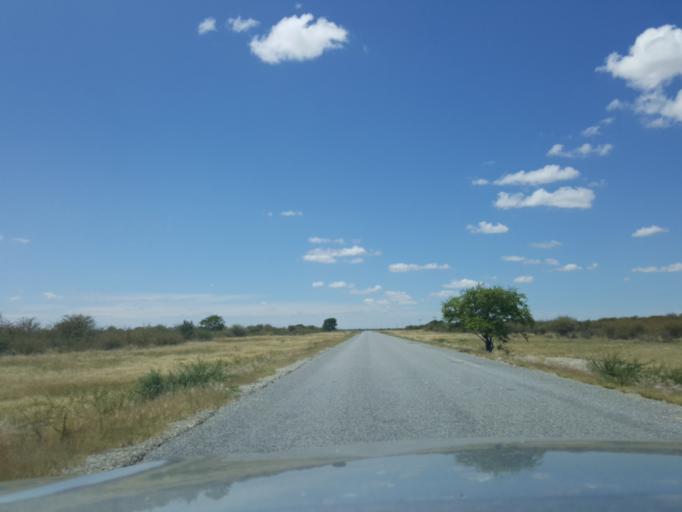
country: BW
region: Central
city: Gweta
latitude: -20.1371
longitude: 25.6623
